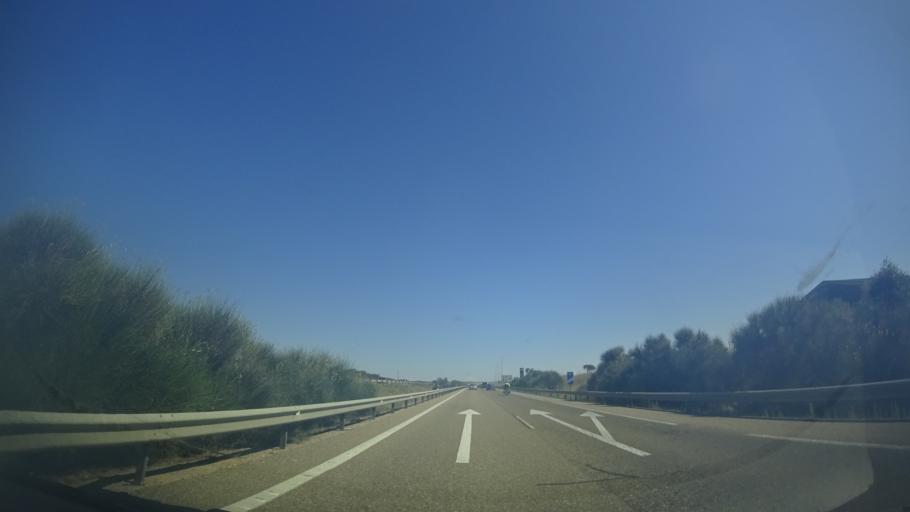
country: ES
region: Castille and Leon
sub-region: Provincia de Valladolid
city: San Pedro de Latarce
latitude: 41.7792
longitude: -5.3174
